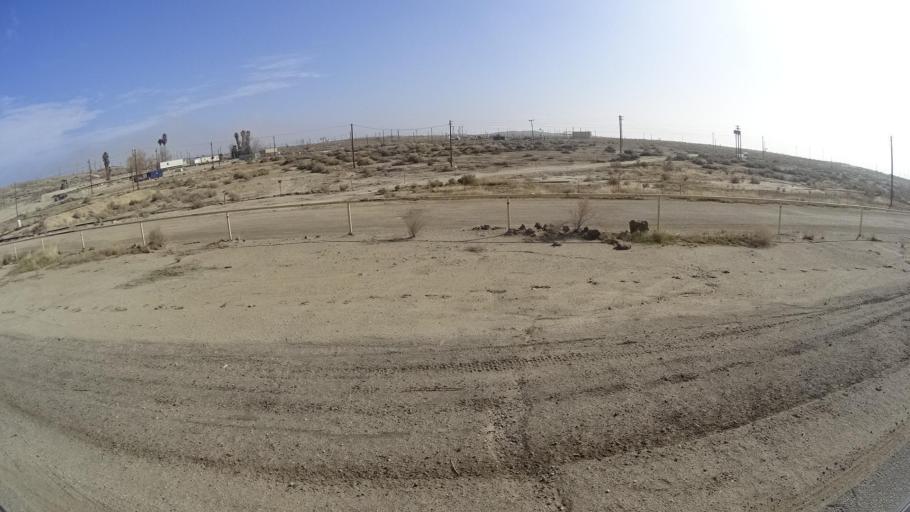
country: US
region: California
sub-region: Kern County
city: Ford City
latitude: 35.1611
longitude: -119.4217
